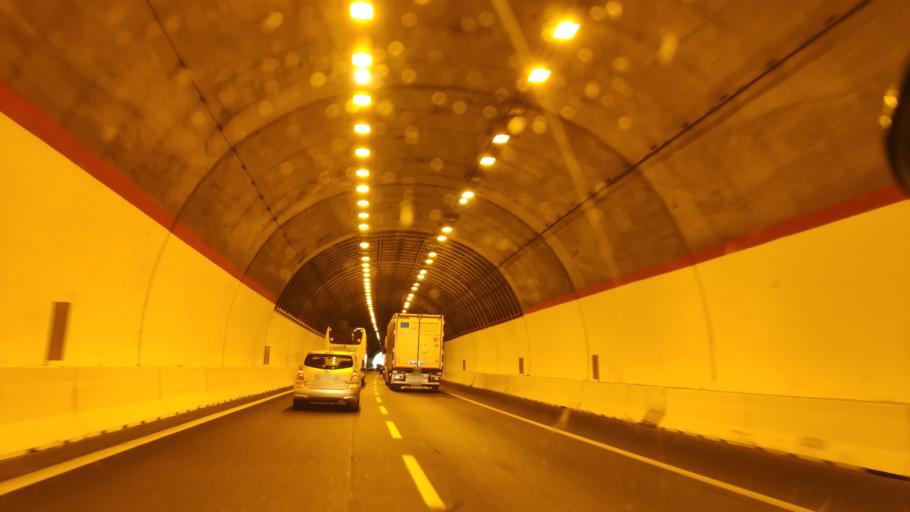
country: IT
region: Campania
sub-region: Provincia di Salerno
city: Pertosa
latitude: 40.5335
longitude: 15.4615
